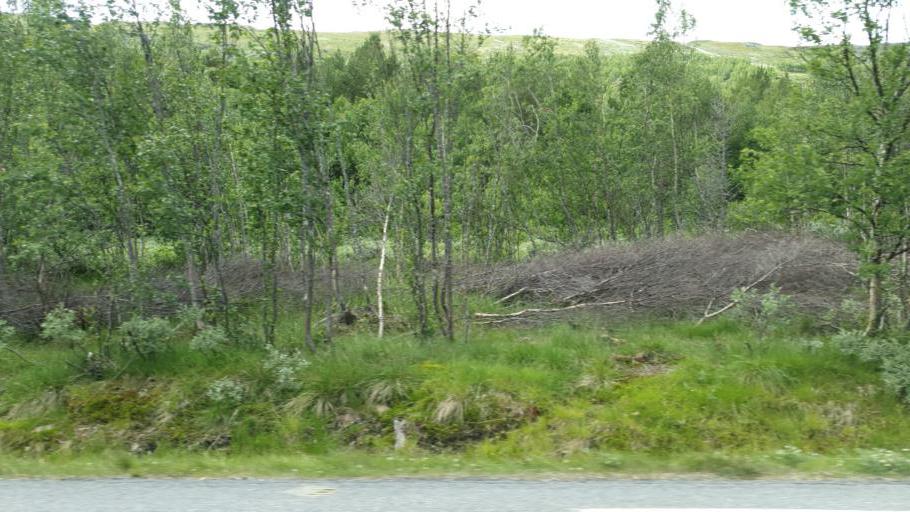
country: NO
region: Oppland
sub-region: Vaga
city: Vagamo
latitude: 61.7523
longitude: 9.0762
